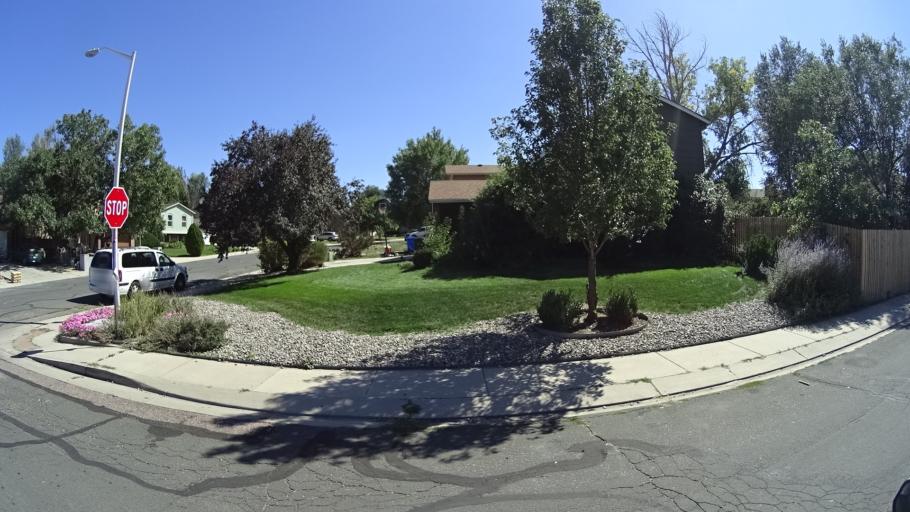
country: US
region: Colorado
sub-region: El Paso County
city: Stratmoor
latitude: 38.7862
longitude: -104.7421
